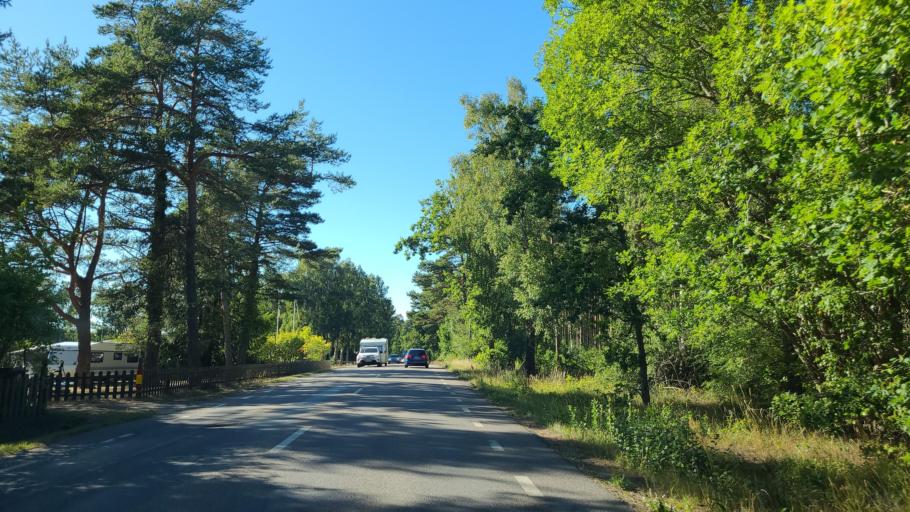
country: SE
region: Kalmar
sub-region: Borgholms Kommun
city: Borgholm
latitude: 57.2566
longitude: 17.0476
